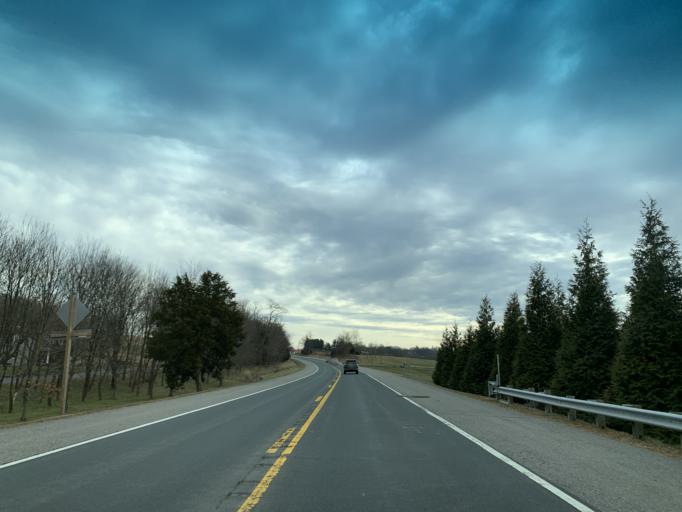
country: US
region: Maryland
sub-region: Washington County
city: Keedysville
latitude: 39.4463
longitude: -77.6653
